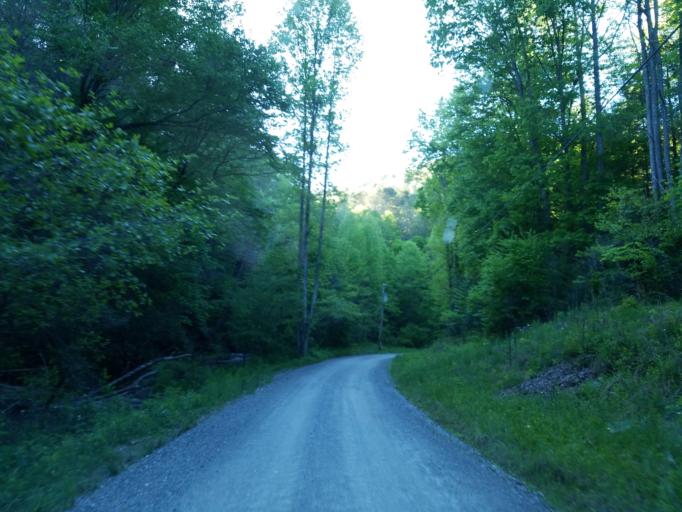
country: US
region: Georgia
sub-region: Fannin County
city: Blue Ridge
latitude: 34.7423
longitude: -84.2911
